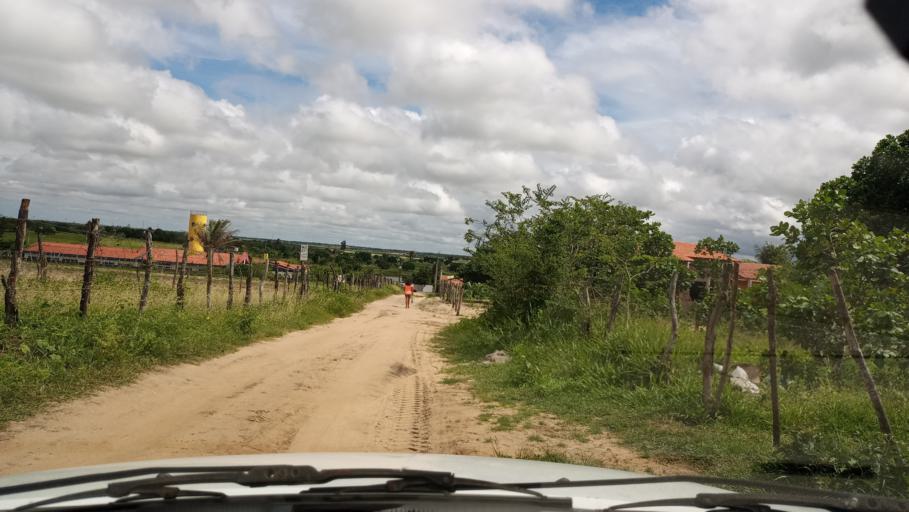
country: BR
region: Rio Grande do Norte
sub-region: Brejinho
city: Brejinho
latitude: -6.1544
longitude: -35.4372
